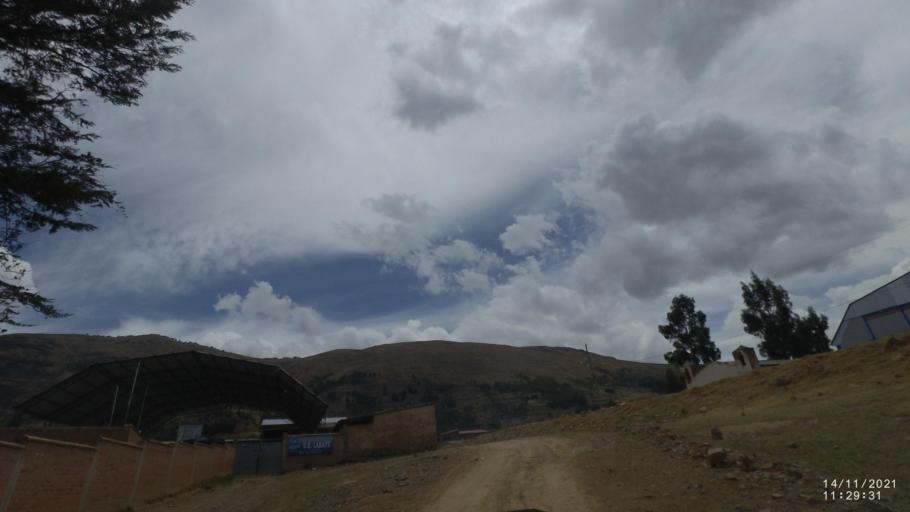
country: BO
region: Cochabamba
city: Colomi
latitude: -17.3442
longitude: -66.0123
